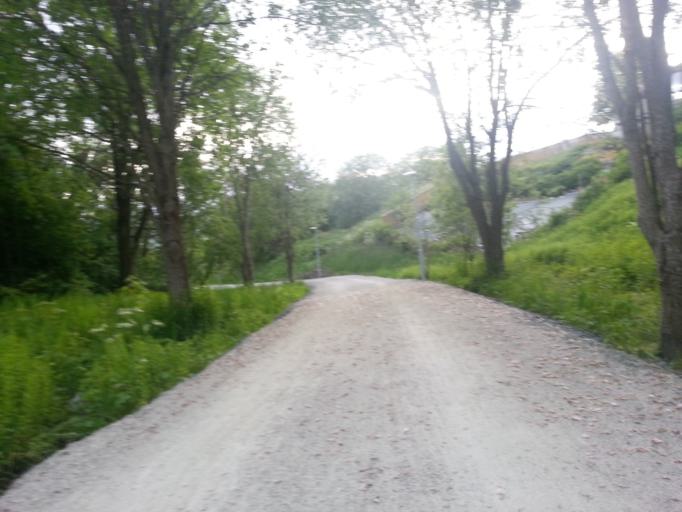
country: NO
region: Sor-Trondelag
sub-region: Trondheim
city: Trondheim
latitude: 63.4140
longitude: 10.4281
